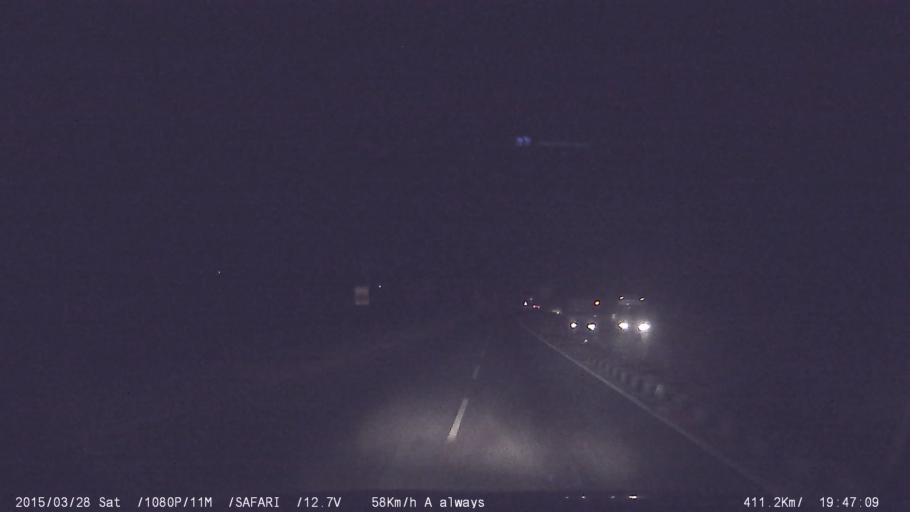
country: IN
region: Karnataka
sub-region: Mandya
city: Pandavapura
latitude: 12.4888
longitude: 76.7820
